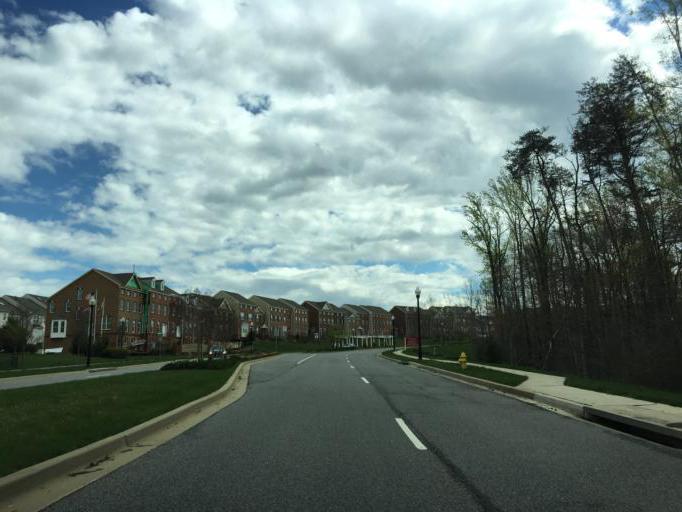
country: US
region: Maryland
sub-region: Anne Arundel County
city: Jessup
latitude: 39.1494
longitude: -76.7463
